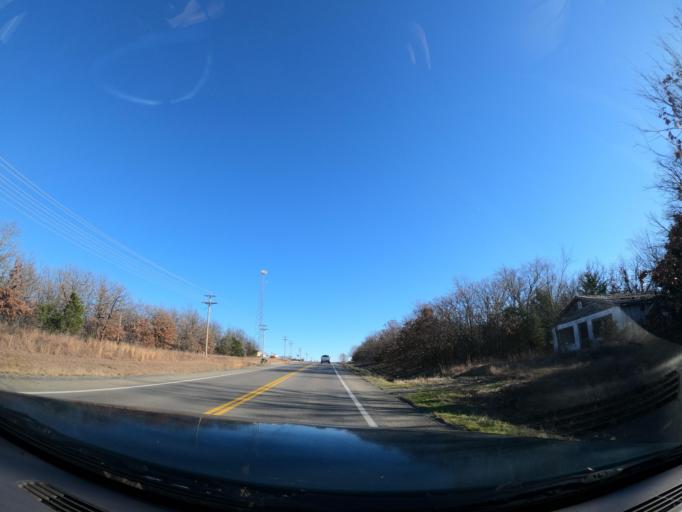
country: US
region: Oklahoma
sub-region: Pittsburg County
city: Longtown
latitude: 35.2370
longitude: -95.4671
